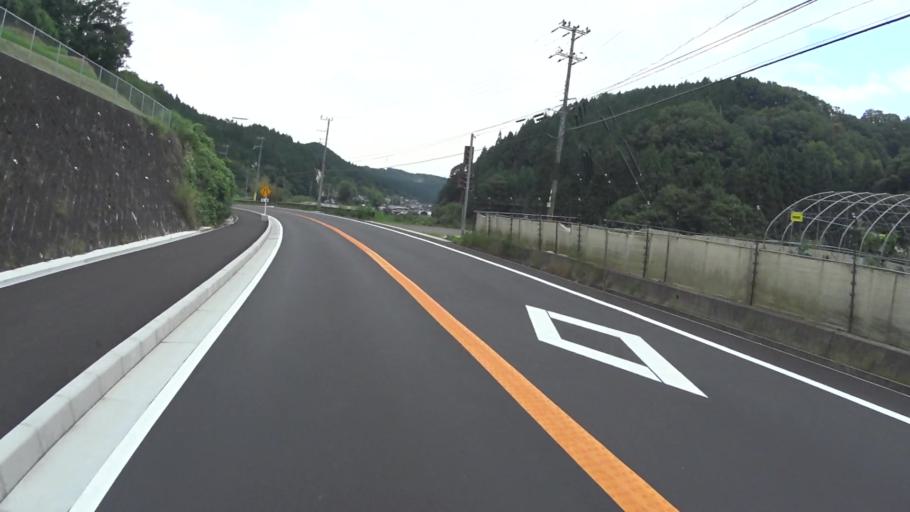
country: JP
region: Kyoto
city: Uji
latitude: 34.8521
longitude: 135.9279
